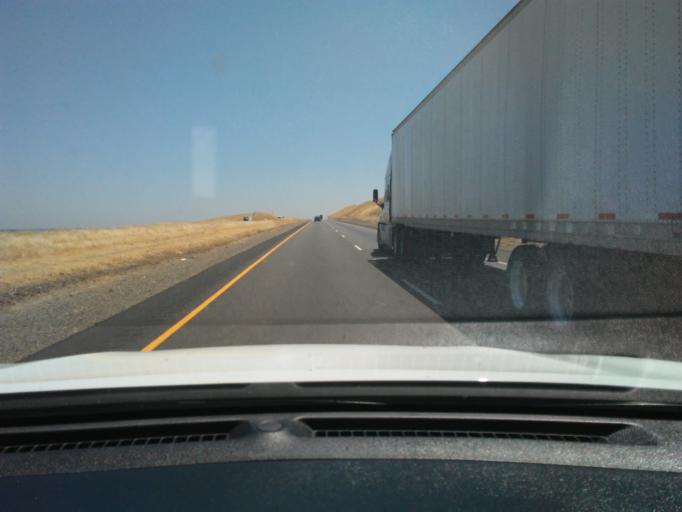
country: US
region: California
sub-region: Stanislaus County
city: Patterson
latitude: 37.4362
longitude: -121.1608
